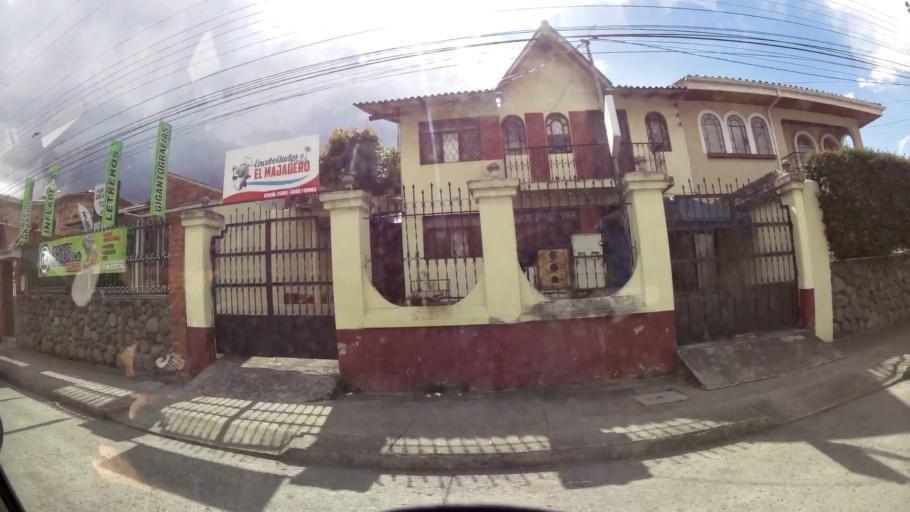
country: EC
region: Azuay
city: Cuenca
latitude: -2.8861
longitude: -79.0024
